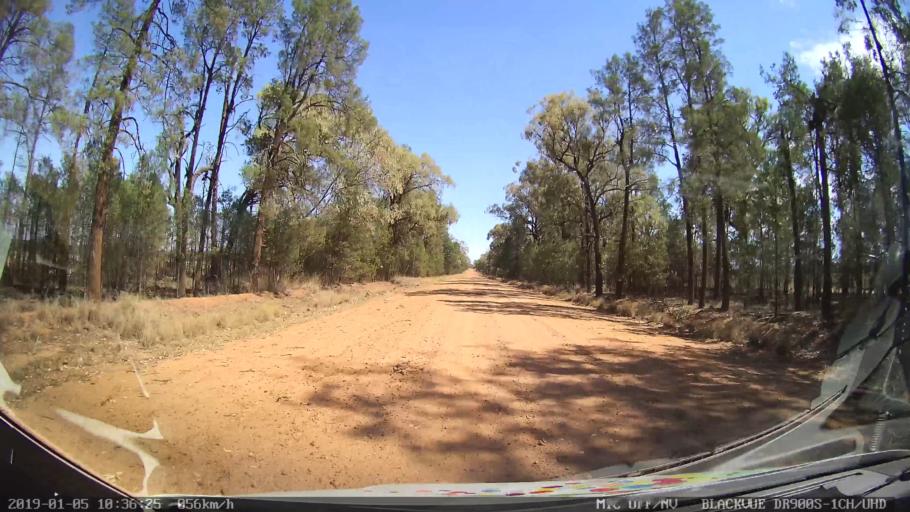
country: AU
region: New South Wales
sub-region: Gilgandra
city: Gilgandra
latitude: -31.4823
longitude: 148.9251
